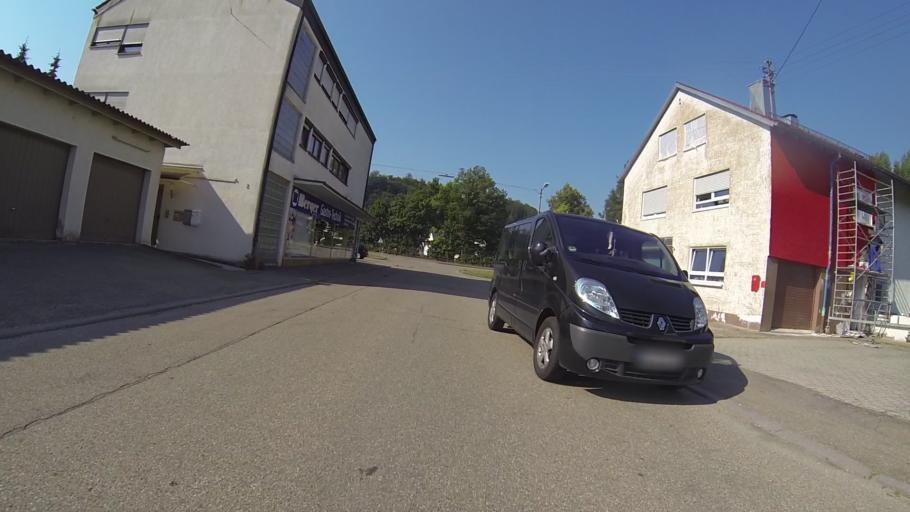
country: DE
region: Baden-Wuerttemberg
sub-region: Regierungsbezirk Stuttgart
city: Konigsbronn
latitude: 48.7453
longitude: 10.1100
